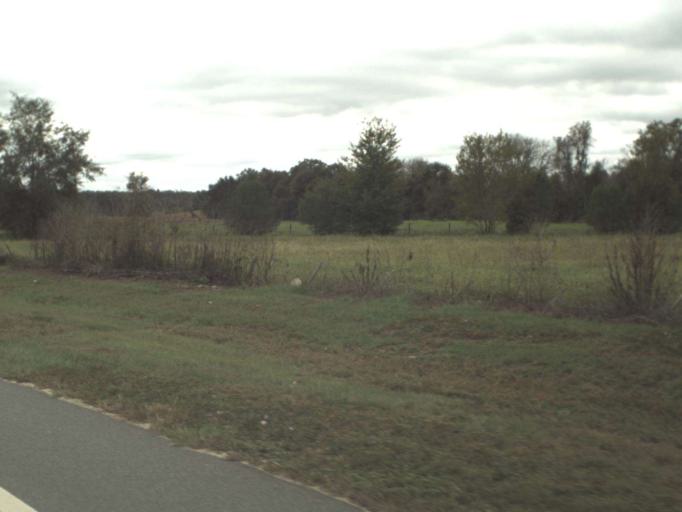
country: US
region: Florida
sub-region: Jackson County
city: Malone
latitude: 30.8367
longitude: -85.0600
